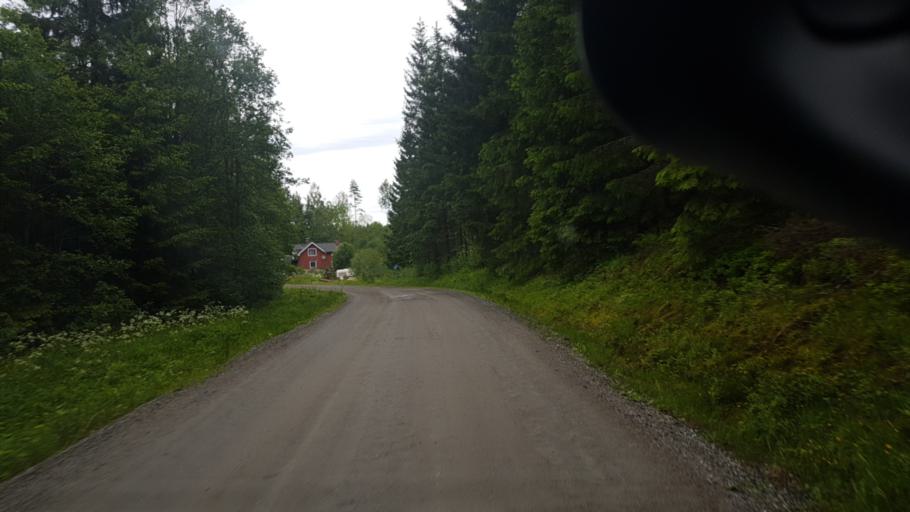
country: NO
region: Ostfold
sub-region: Romskog
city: Romskog
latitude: 59.6956
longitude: 11.9438
